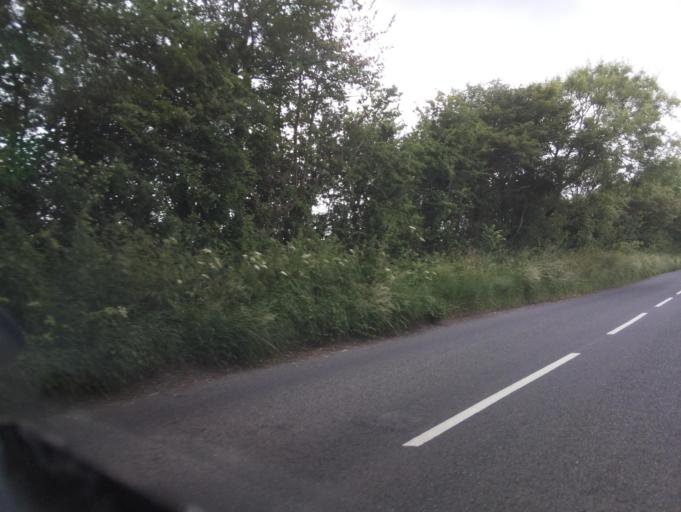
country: GB
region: England
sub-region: South Gloucestershire
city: Pucklechurch
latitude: 51.4756
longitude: -2.4267
